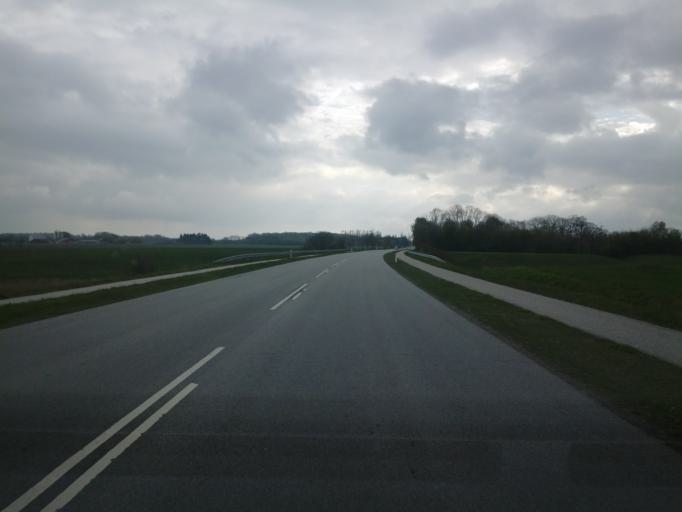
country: DK
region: North Denmark
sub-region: Frederikshavn Kommune
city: Saeby
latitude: 57.3047
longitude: 10.4256
